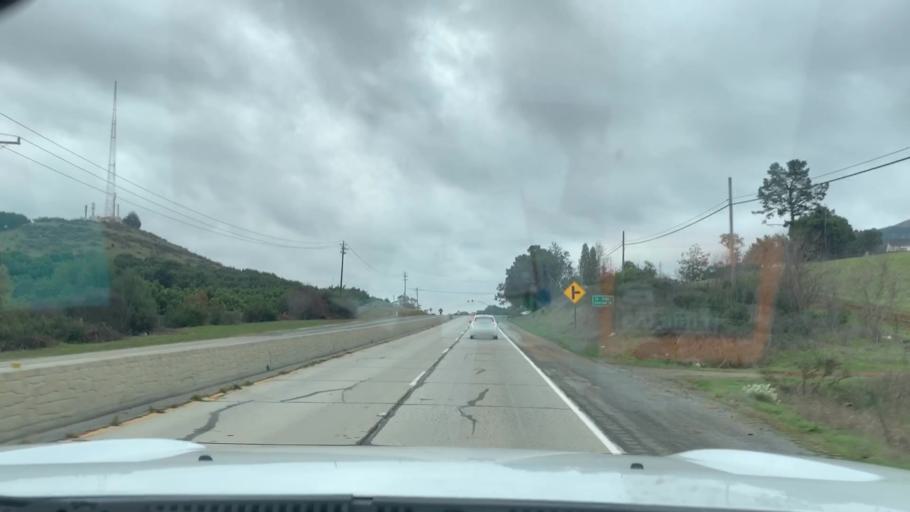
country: US
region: California
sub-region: San Luis Obispo County
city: San Luis Obispo
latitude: 35.3034
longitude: -120.6771
